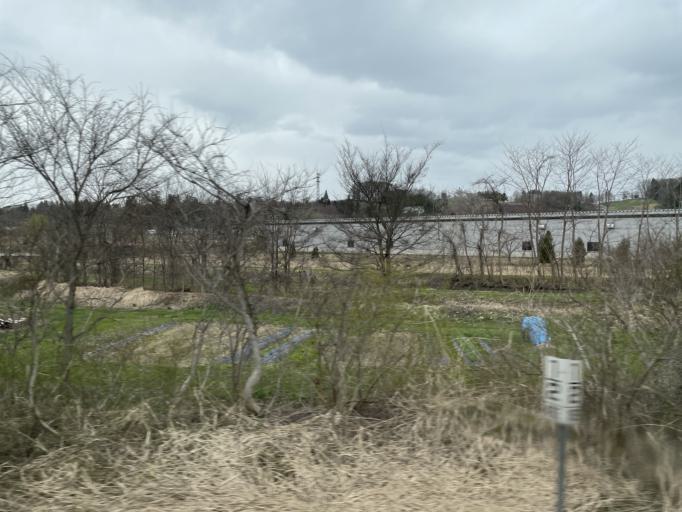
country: JP
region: Aomori
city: Namioka
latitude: 40.7180
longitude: 140.5833
